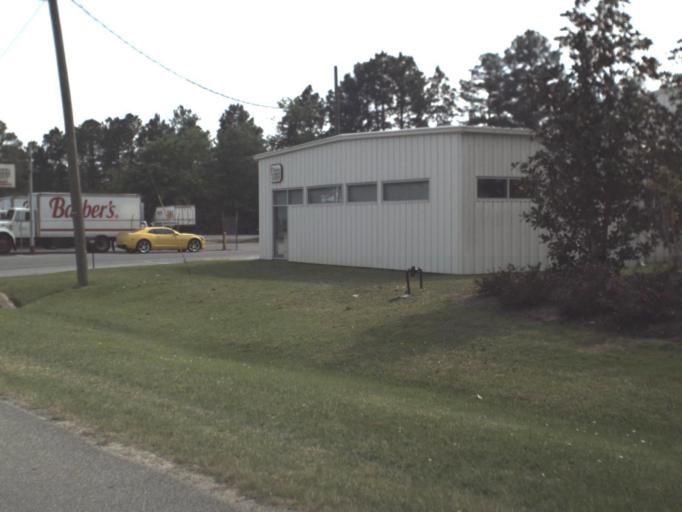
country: US
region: Florida
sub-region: Escambia County
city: Gonzalez
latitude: 30.5505
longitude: -87.2831
